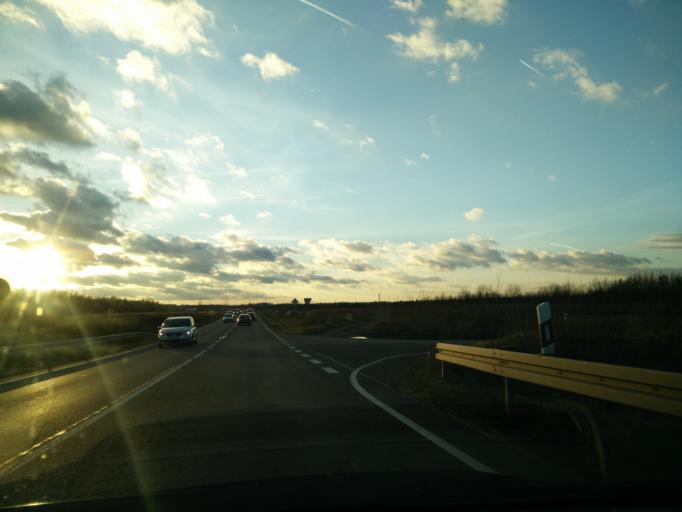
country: DE
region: Saxony
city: Bohlen
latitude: 51.2242
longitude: 12.3819
